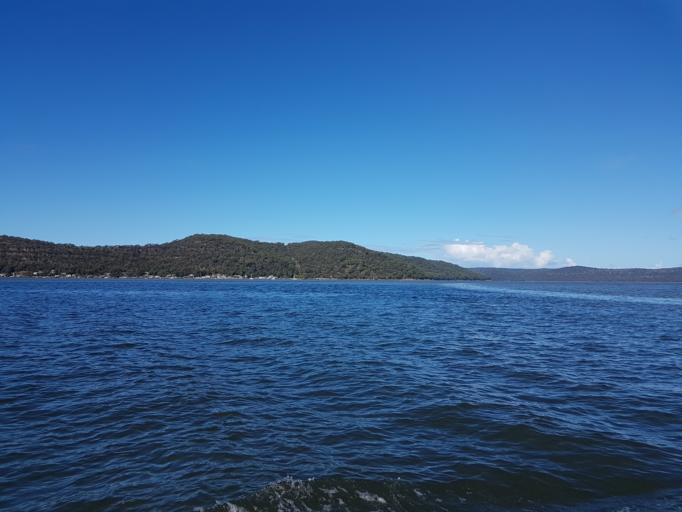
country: AU
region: New South Wales
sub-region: Gosford Shire
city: Umina
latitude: -33.5455
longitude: 151.2324
